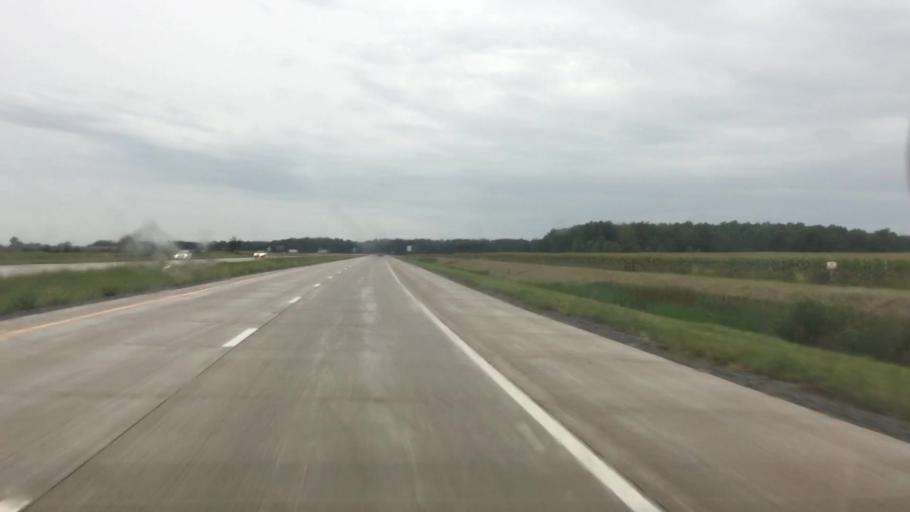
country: US
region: Ohio
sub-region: Paulding County
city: Paulding
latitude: 41.2317
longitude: -84.5542
